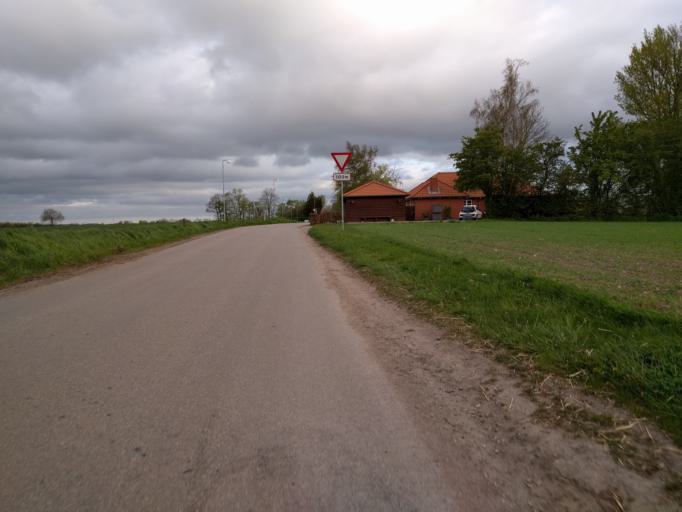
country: DK
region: South Denmark
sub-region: Odense Kommune
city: Bullerup
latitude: 55.4369
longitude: 10.5075
